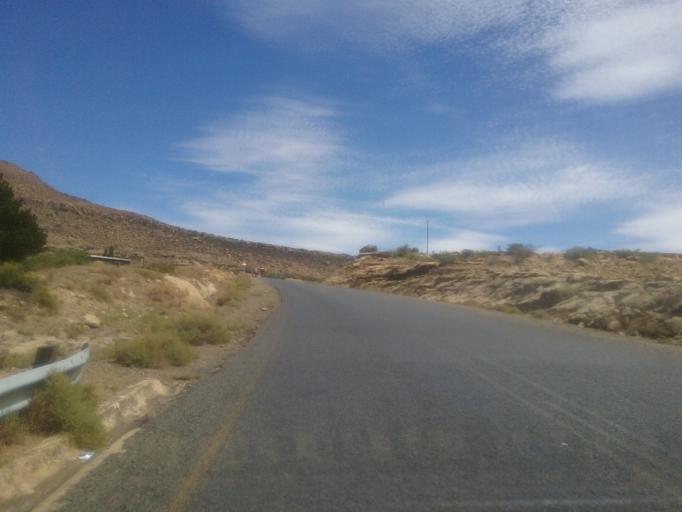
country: LS
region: Mohale's Hoek District
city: Mohale's Hoek
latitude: -30.0768
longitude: 27.4269
